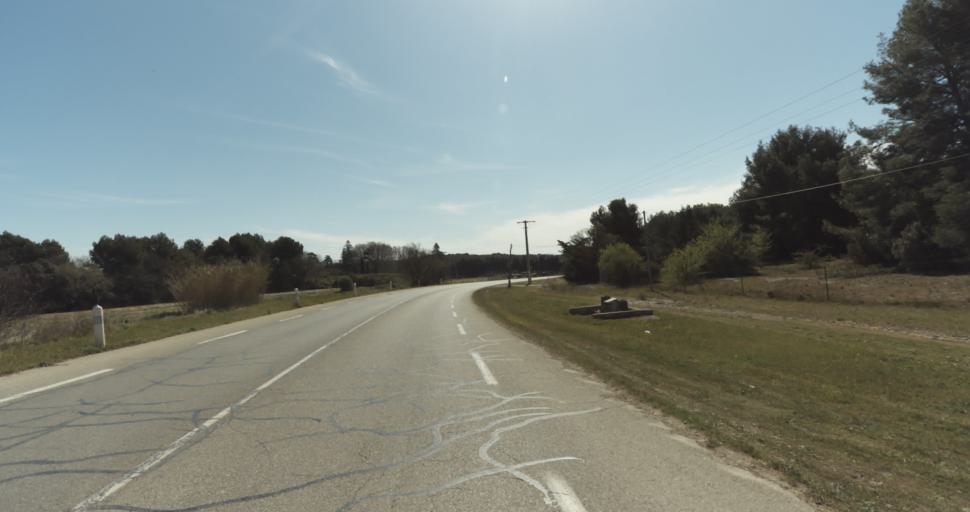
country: FR
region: Provence-Alpes-Cote d'Azur
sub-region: Departement des Bouches-du-Rhone
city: Lambesc
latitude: 43.6671
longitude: 5.2491
